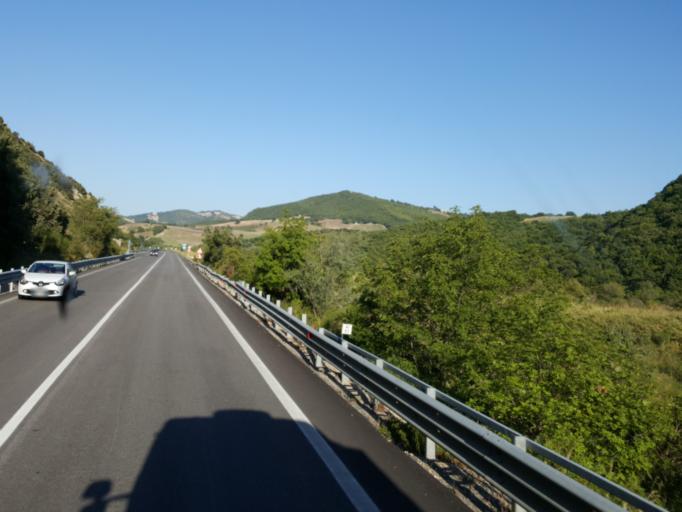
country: IT
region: Molise
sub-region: Provincia di Campobasso
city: Montemitro
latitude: 41.9121
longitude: 14.6544
